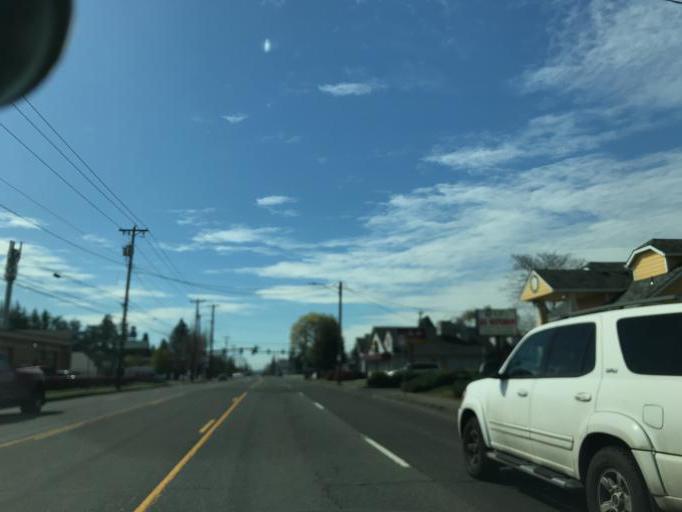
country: US
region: Oregon
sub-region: Multnomah County
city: Lents
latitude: 45.4772
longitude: -122.5791
